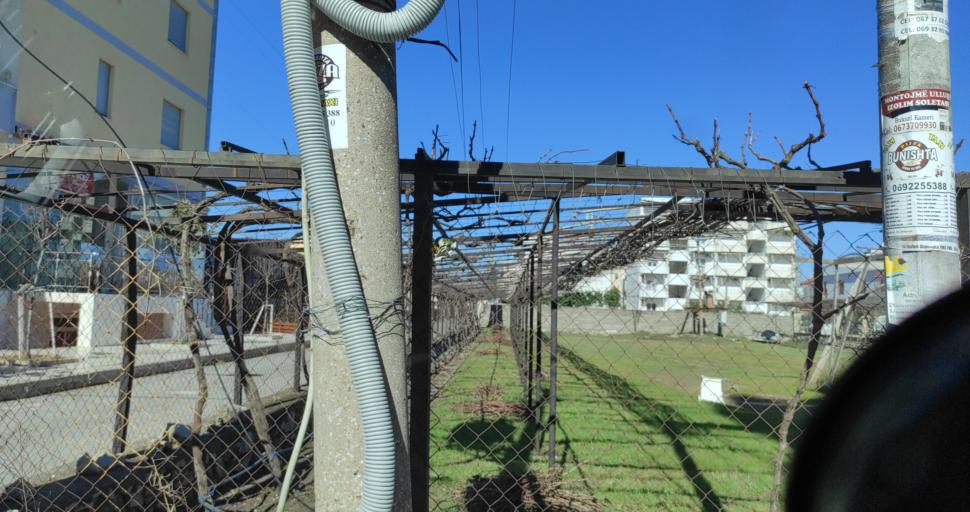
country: AL
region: Shkoder
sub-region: Rrethi i Shkodres
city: Velipoje
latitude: 41.8630
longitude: 19.4300
